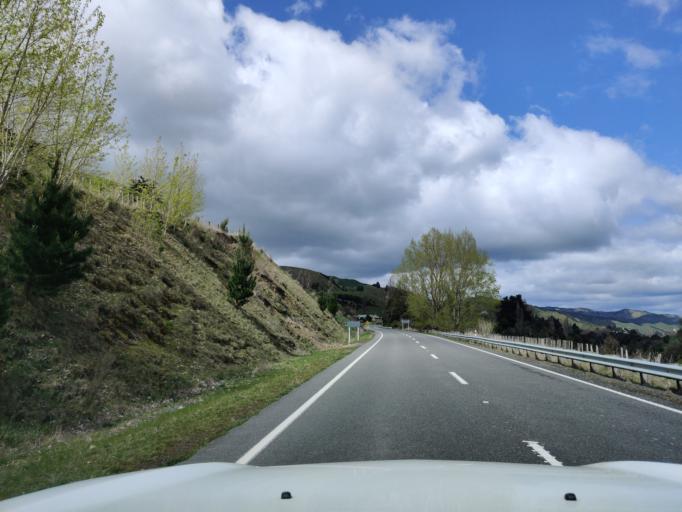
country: NZ
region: Manawatu-Wanganui
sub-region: Ruapehu District
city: Waiouru
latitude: -39.6503
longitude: 175.3257
